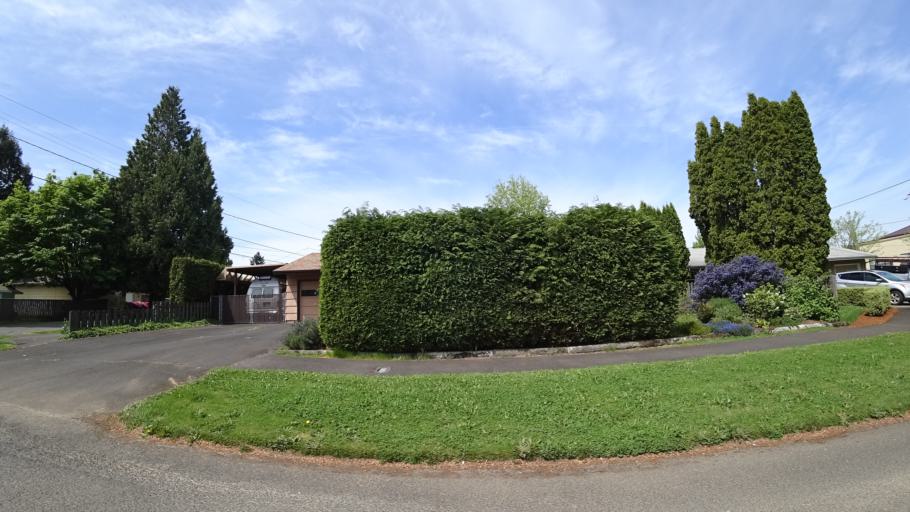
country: US
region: Oregon
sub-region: Clackamas County
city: Milwaukie
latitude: 45.4468
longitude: -122.6169
